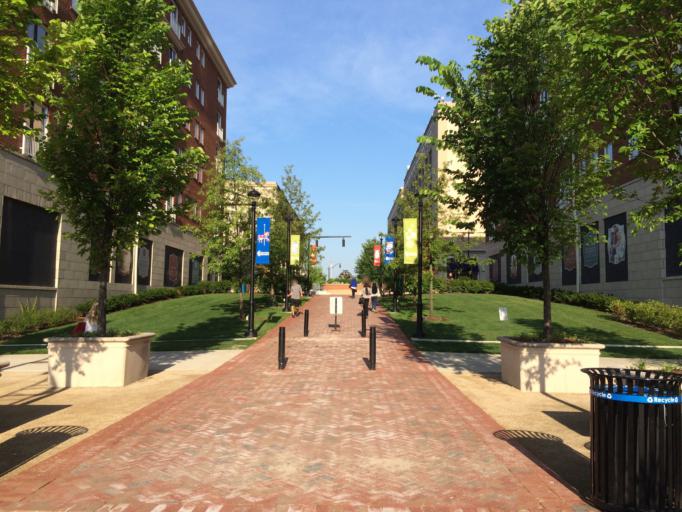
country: US
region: Ohio
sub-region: Franklin County
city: Columbus
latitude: 39.9590
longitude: -82.9991
